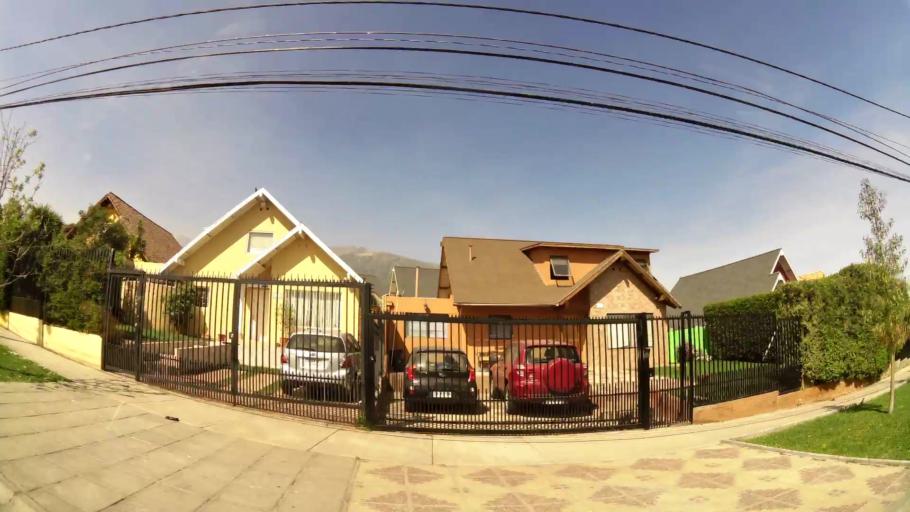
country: CL
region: Santiago Metropolitan
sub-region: Provincia de Cordillera
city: Puente Alto
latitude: -33.5359
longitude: -70.5519
